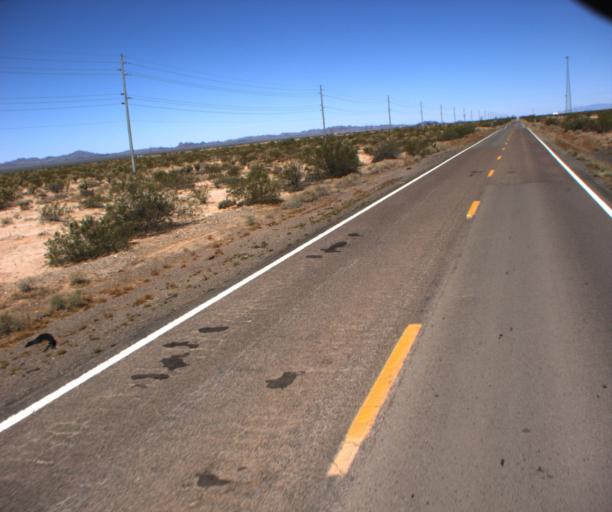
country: US
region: Arizona
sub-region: La Paz County
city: Salome
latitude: 33.8329
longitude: -113.8791
